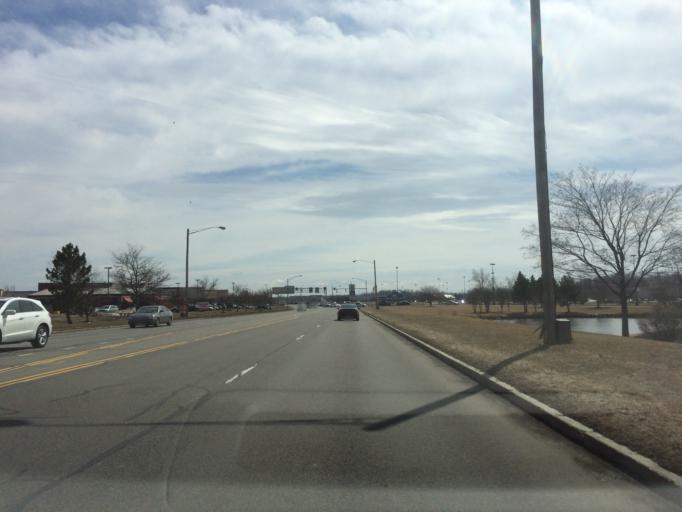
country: US
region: New York
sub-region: Monroe County
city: Rochester
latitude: 43.0820
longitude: -77.6298
